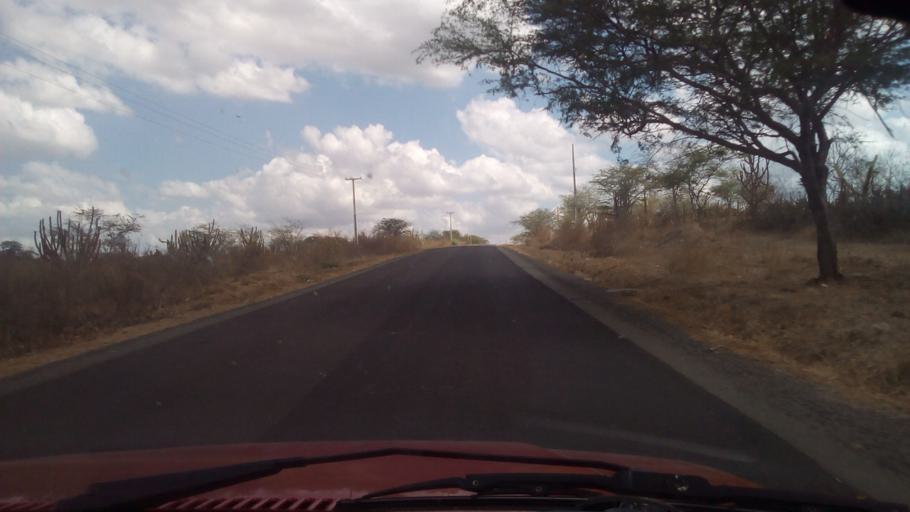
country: BR
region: Paraiba
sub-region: Cacimba De Dentro
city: Cacimba de Dentro
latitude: -6.7102
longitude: -35.7240
